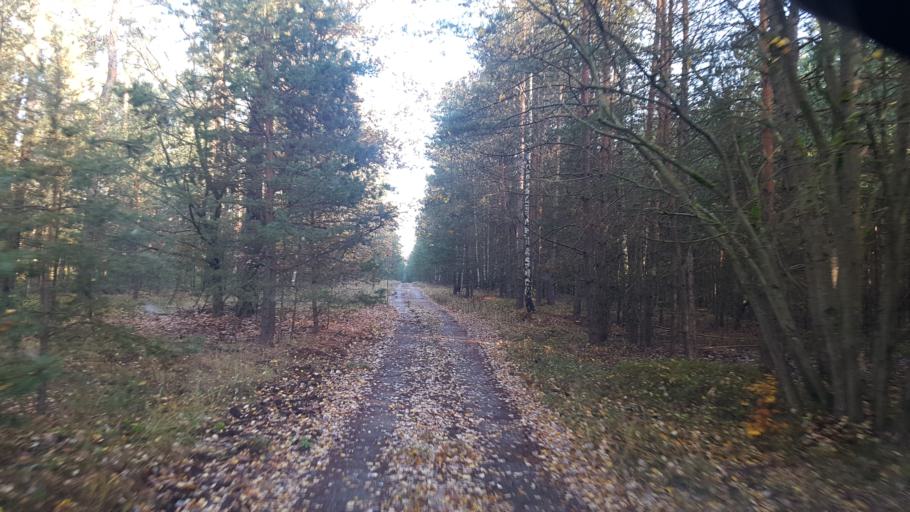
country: DE
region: Brandenburg
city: Crinitz
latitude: 51.7214
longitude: 13.7448
